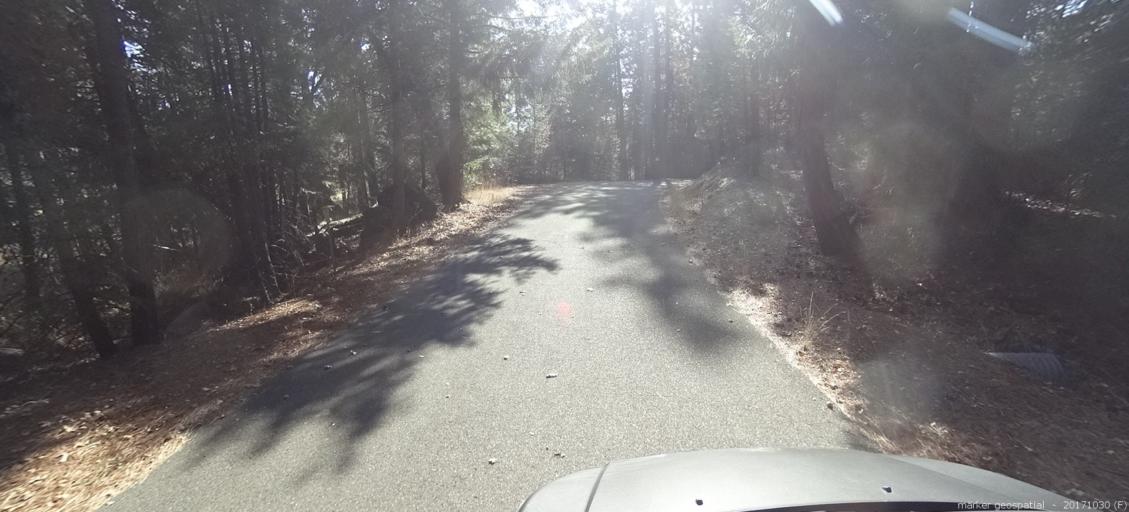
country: US
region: California
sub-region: Shasta County
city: Shingletown
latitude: 40.5078
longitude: -121.7373
